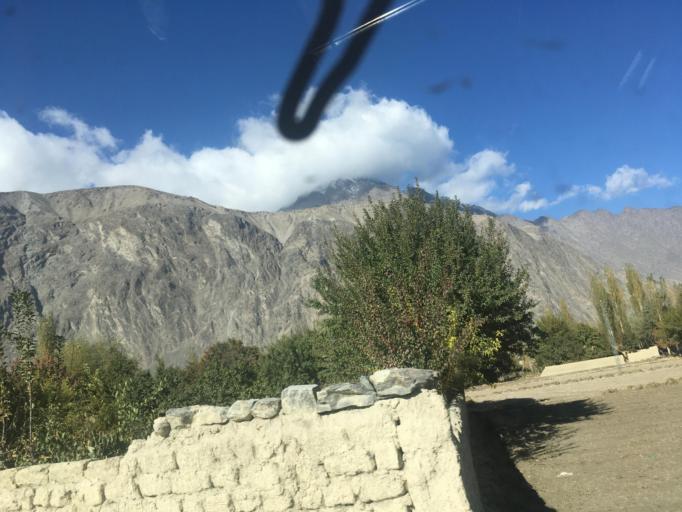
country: PK
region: Gilgit-Baltistan
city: Skardu
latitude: 35.3488
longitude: 75.5234
